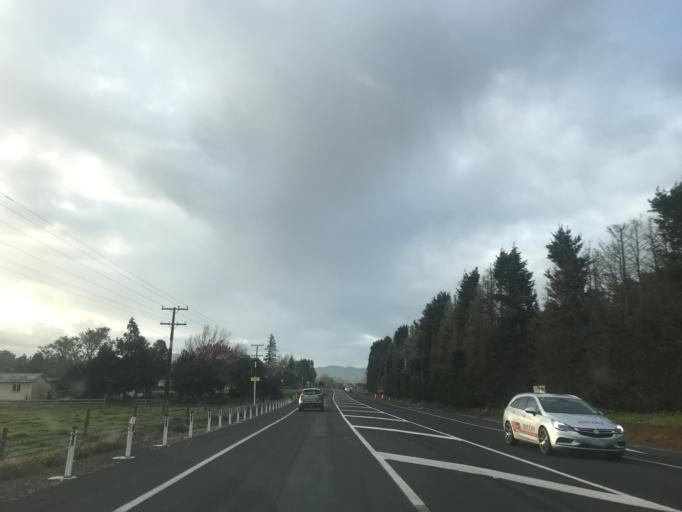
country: NZ
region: Waikato
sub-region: Hauraki District
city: Waihi
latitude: -37.4295
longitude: 175.8712
